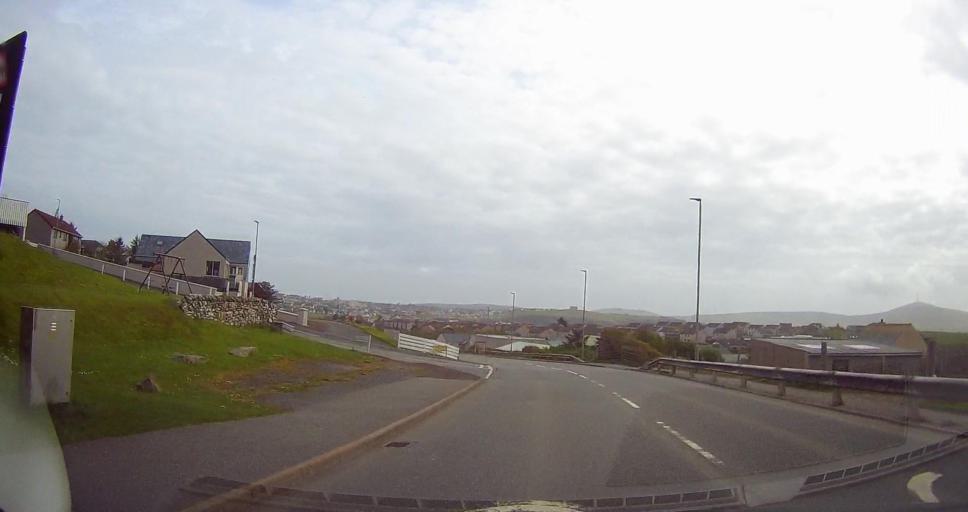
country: GB
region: Scotland
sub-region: Shetland Islands
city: Lerwick
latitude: 60.1443
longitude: -1.1750
